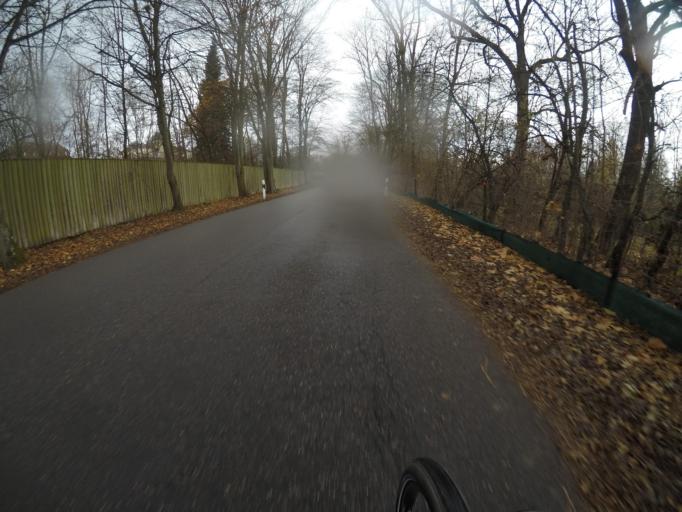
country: DE
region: Baden-Wuerttemberg
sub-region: Regierungsbezirk Stuttgart
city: Gerlingen
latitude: 48.7869
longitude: 9.0871
